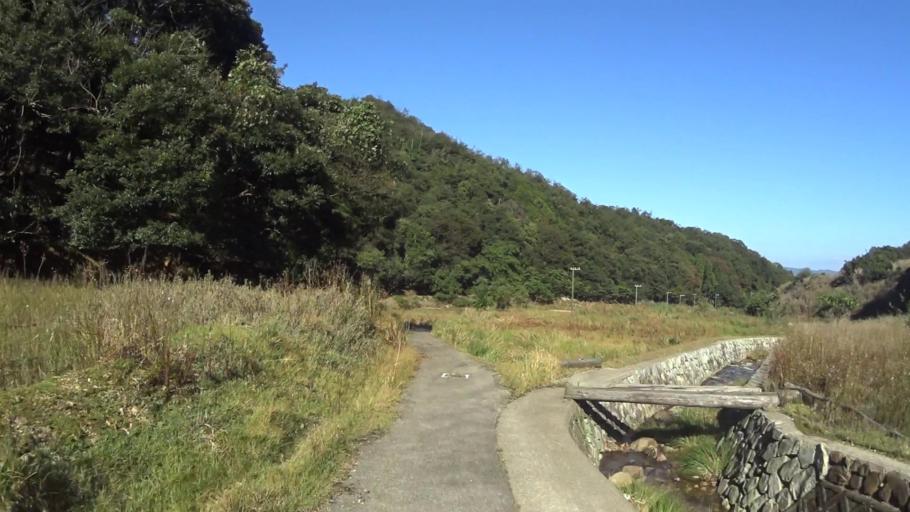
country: JP
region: Hyogo
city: Toyooka
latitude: 35.6467
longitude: 134.8741
